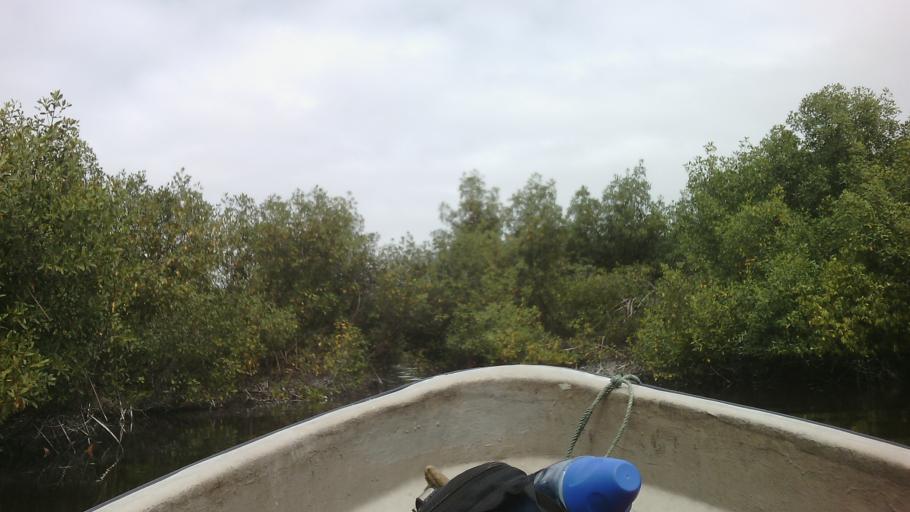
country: BJ
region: Atlantique
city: Hevie
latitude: 6.3503
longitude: 2.2903
